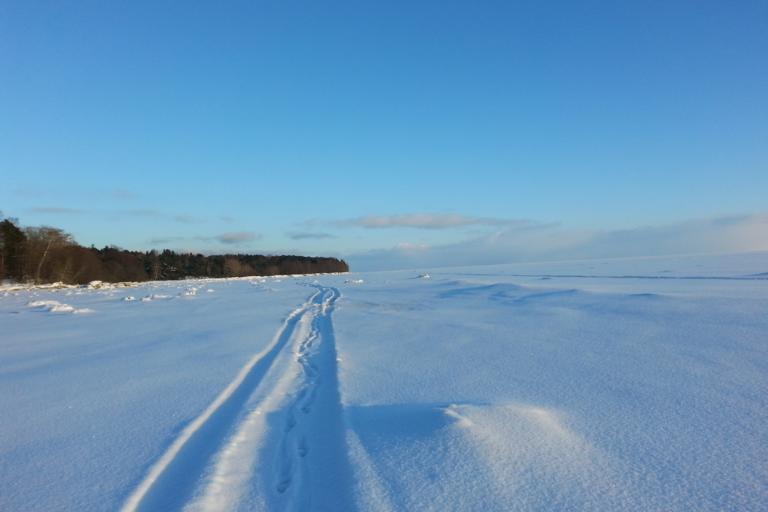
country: RU
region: Leningrad
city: Roshchino
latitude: 60.1953
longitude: 29.6102
